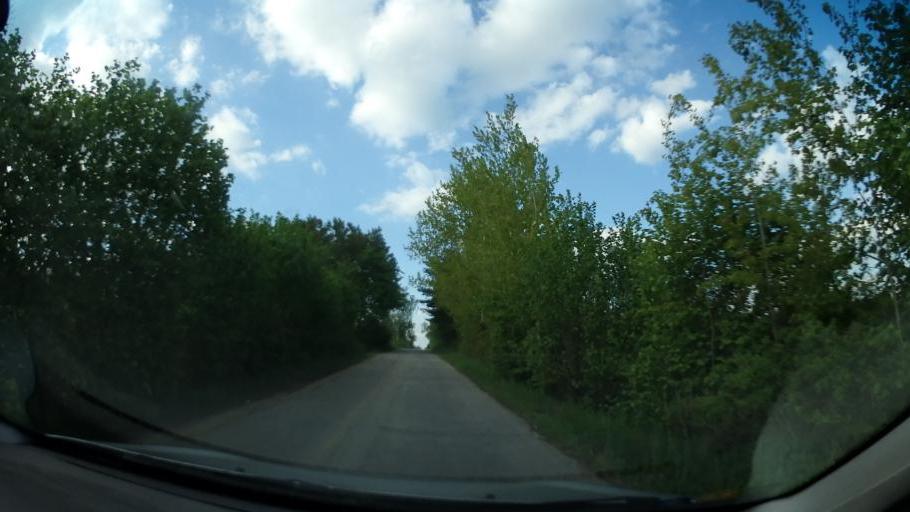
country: CZ
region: Vysocina
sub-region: Okres Zd'ar nad Sazavou
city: Velke Mezirici
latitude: 49.3461
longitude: 15.9604
